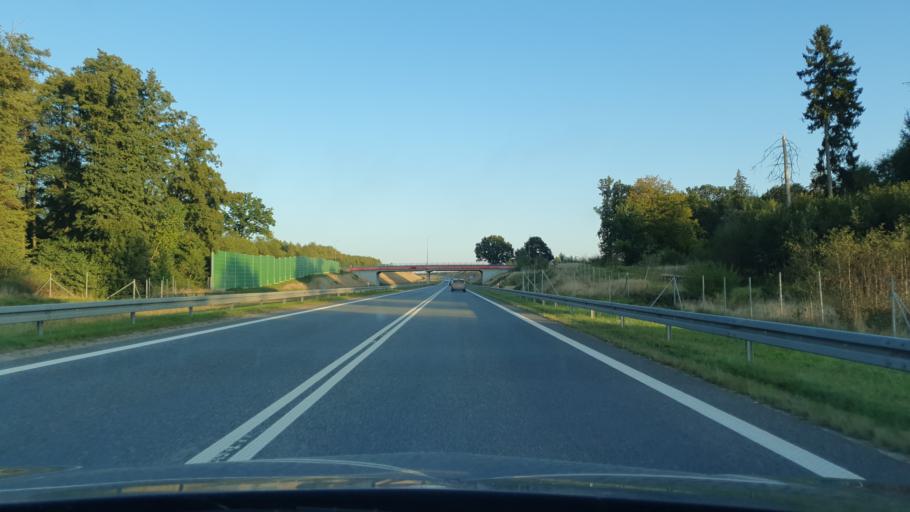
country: PL
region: Pomeranian Voivodeship
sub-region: Powiat slupski
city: Kobylnica
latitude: 54.4314
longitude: 16.9729
